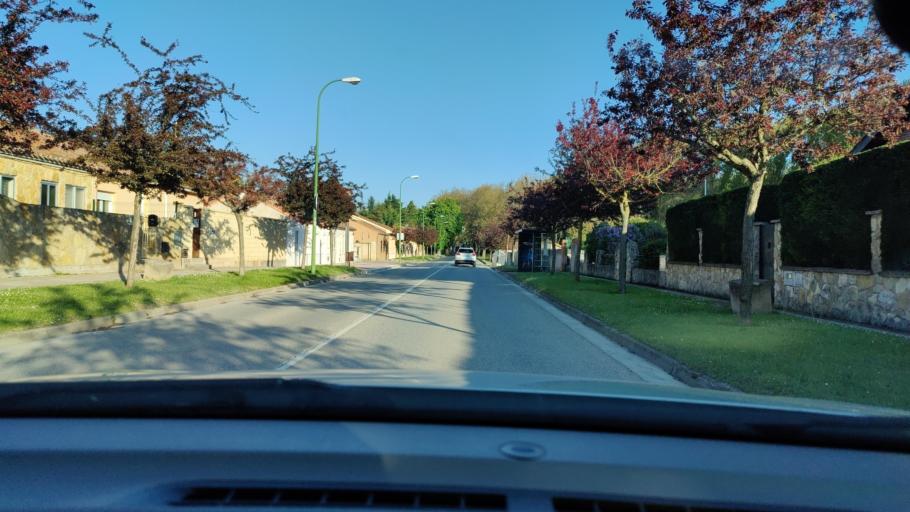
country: ES
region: Castille and Leon
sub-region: Provincia de Burgos
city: Villagonzalo-Pedernales
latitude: 42.3474
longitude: -3.7312
